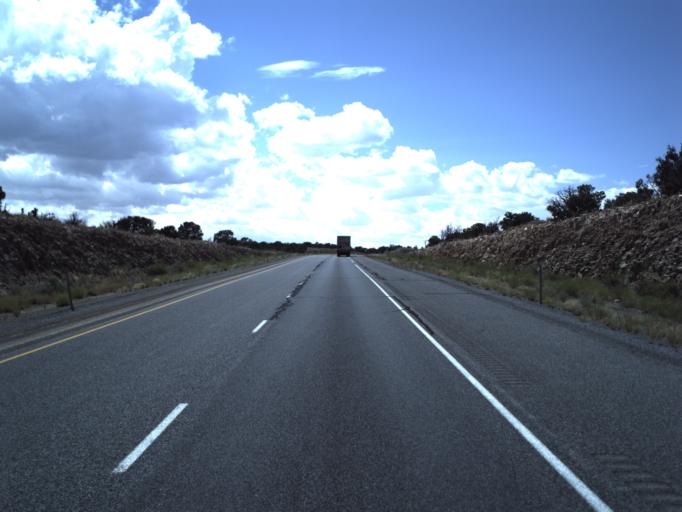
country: US
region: Utah
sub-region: Emery County
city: Castle Dale
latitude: 38.8997
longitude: -110.5730
